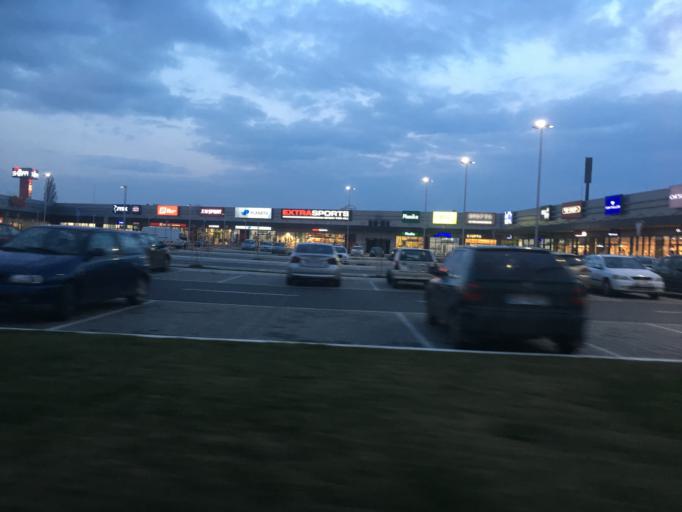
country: RS
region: Central Serbia
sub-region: Belgrade
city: Stari Grad
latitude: 44.8879
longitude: 20.4582
